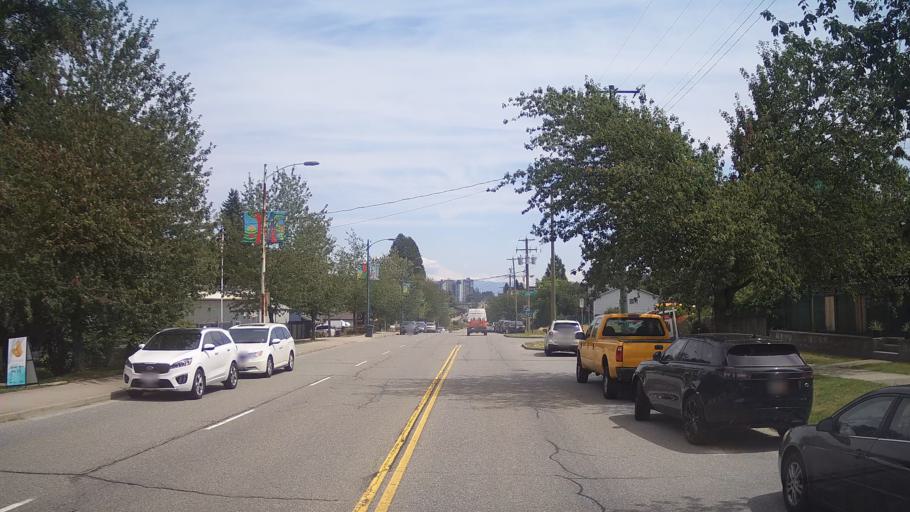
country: CA
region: British Columbia
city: Port Moody
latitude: 49.2777
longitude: -122.8625
